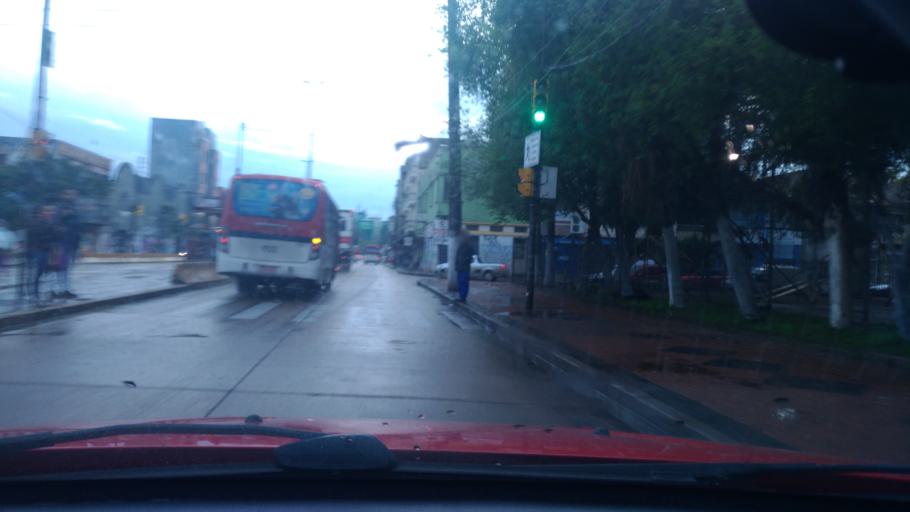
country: BR
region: Rio Grande do Sul
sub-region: Porto Alegre
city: Porto Alegre
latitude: -30.0206
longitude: -51.2107
